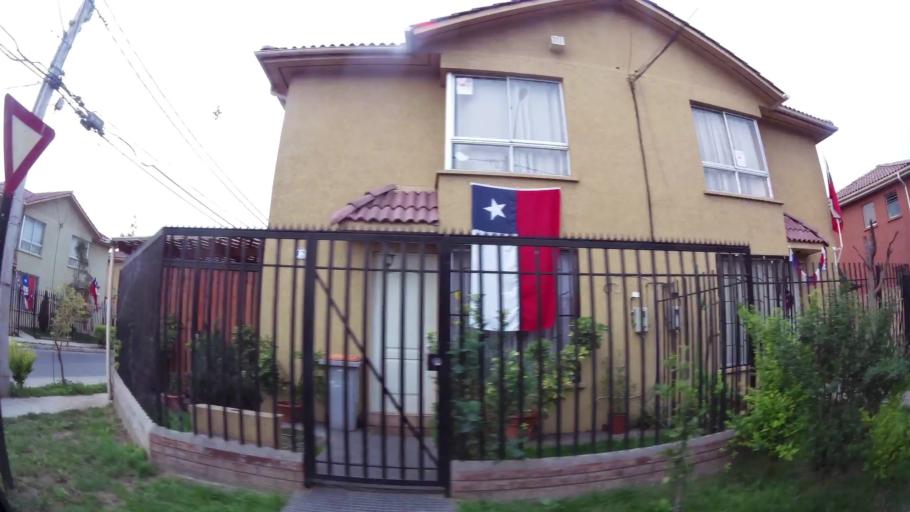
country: CL
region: Santiago Metropolitan
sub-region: Provincia de Talagante
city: Penaflor
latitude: -33.5321
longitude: -70.7978
